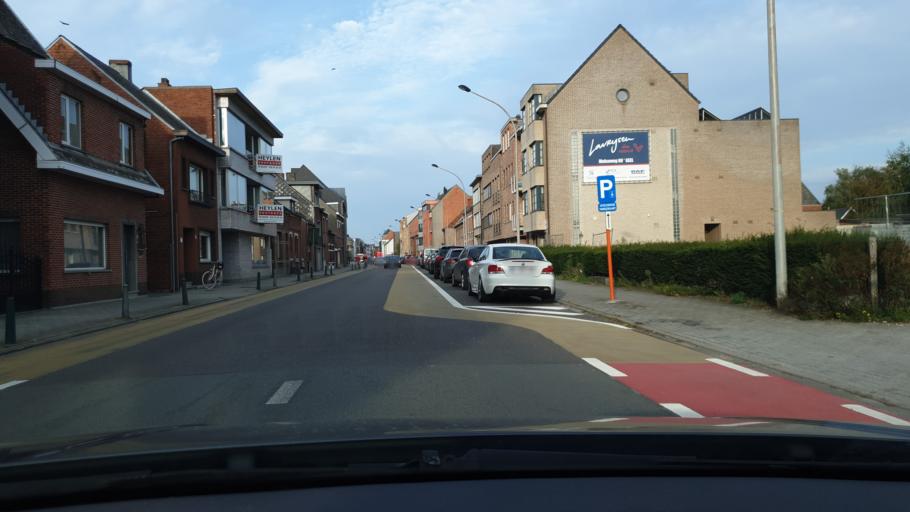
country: BE
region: Flanders
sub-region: Provincie Antwerpen
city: Geel
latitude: 51.1575
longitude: 4.9943
